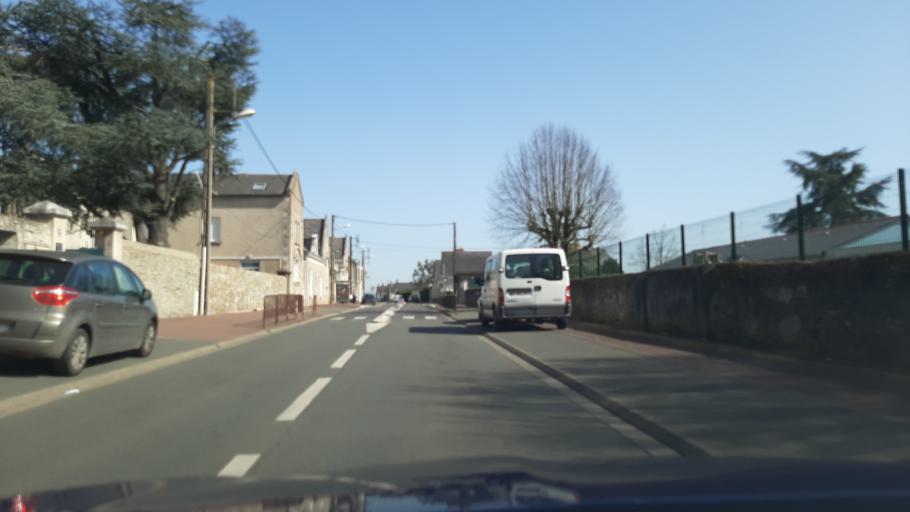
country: FR
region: Pays de la Loire
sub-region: Departement de Maine-et-Loire
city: Les Ponts-de-Ce
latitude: 47.4534
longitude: -0.5194
